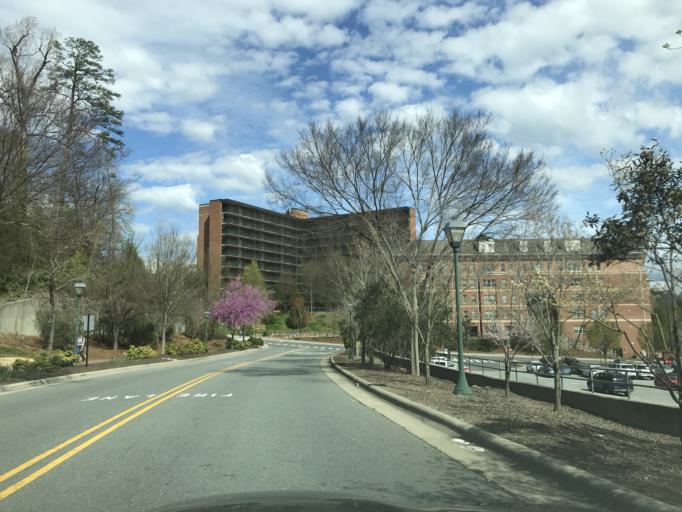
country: US
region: North Carolina
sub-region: Orange County
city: Chapel Hill
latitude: 35.9019
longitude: -79.0453
